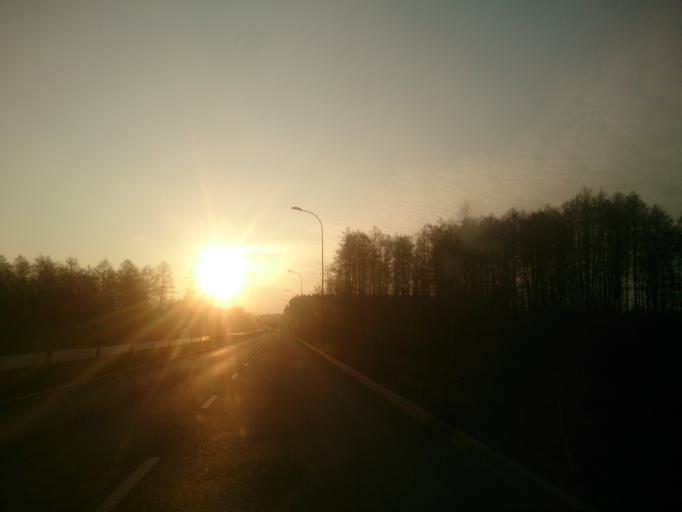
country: PL
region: Kujawsko-Pomorskie
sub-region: Powiat brodnicki
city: Brodnica
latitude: 53.2435
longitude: 19.3766
